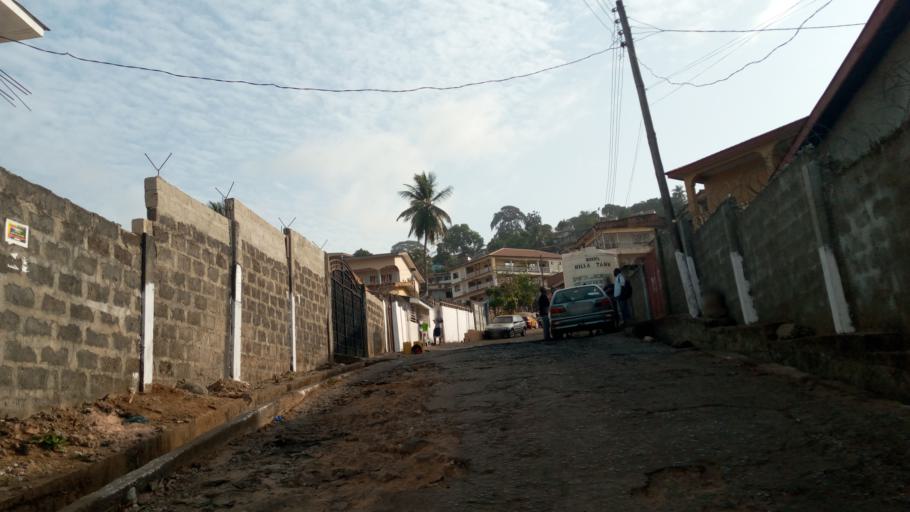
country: SL
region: Western Area
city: Freetown
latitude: 8.4751
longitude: -13.2559
